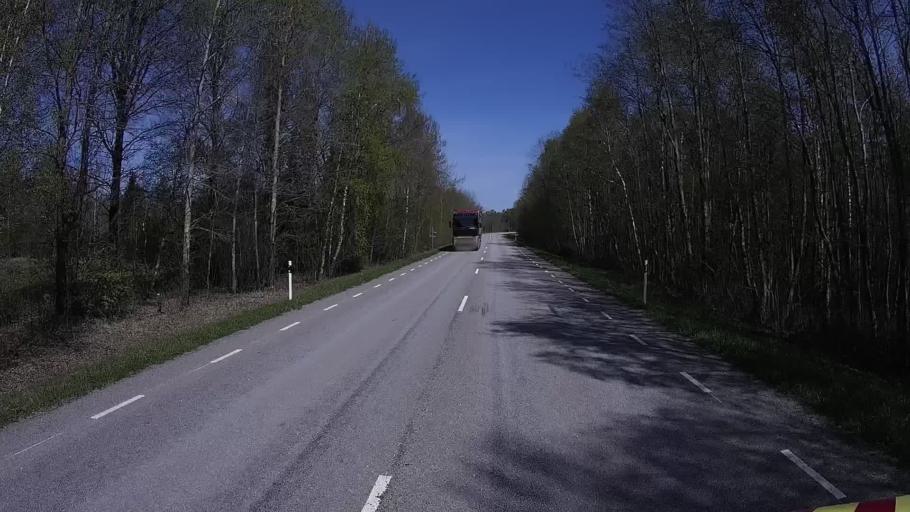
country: EE
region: Laeaene
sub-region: Ridala Parish
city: Uuemoisa
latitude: 58.9783
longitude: 23.6813
